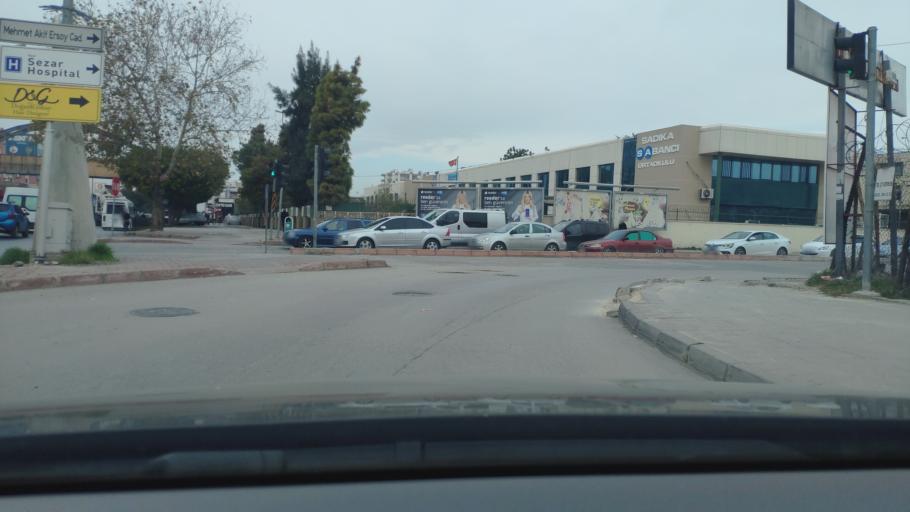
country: TR
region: Adana
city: Seyhan
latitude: 36.9945
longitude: 35.2880
